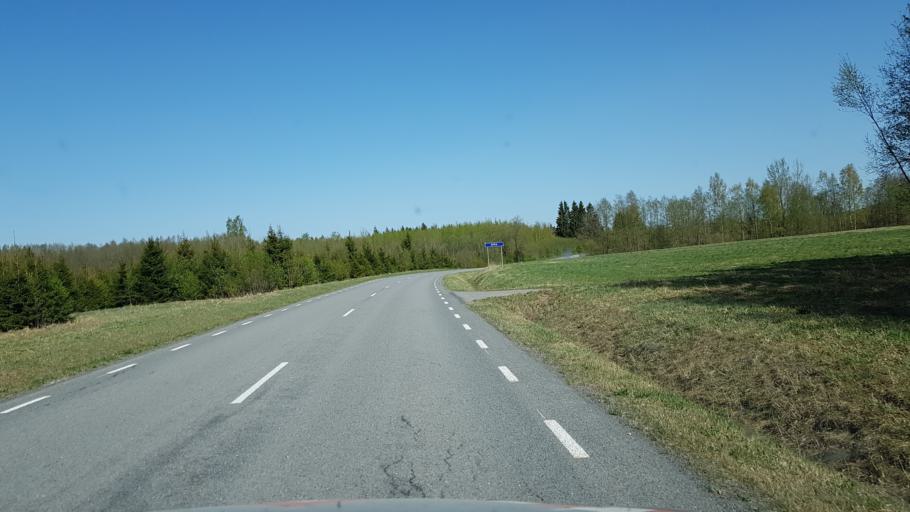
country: EE
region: Viljandimaa
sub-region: Suure-Jaani vald
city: Suure-Jaani
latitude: 58.4857
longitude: 25.4447
